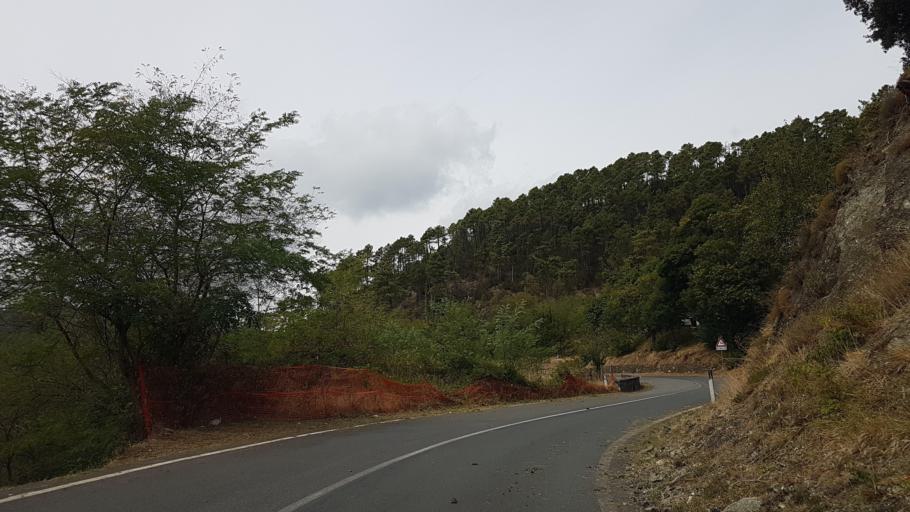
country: IT
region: Liguria
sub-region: Provincia di La Spezia
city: Carrodano
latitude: 44.2477
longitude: 9.6147
